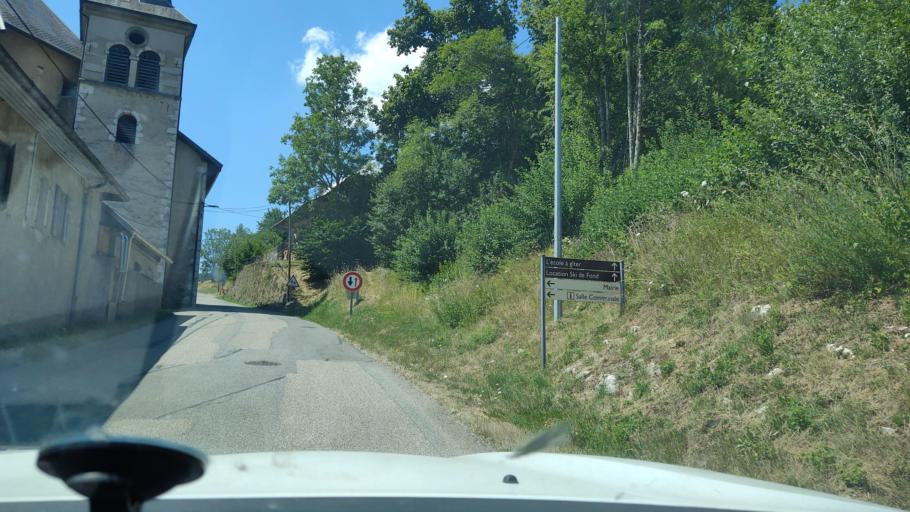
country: FR
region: Rhone-Alpes
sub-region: Departement de la Haute-Savoie
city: Cusy
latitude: 45.6821
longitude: 6.0560
